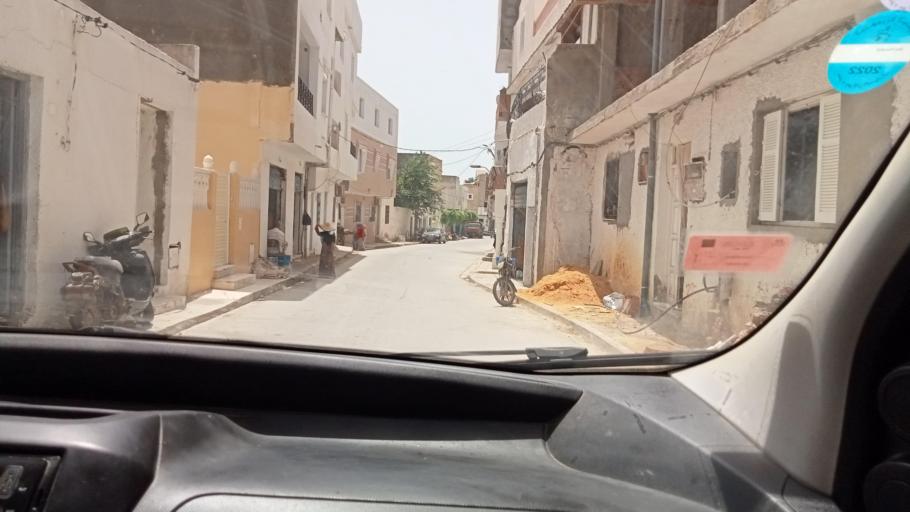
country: TN
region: Nabul
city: Qulaybiyah
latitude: 36.8529
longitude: 11.0890
